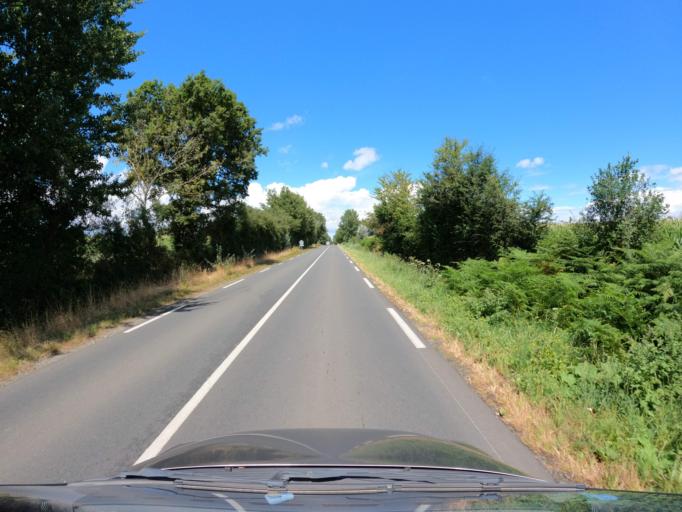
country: FR
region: Pays de la Loire
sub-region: Departement de la Sarthe
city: Brulon
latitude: 47.9349
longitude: -0.2588
